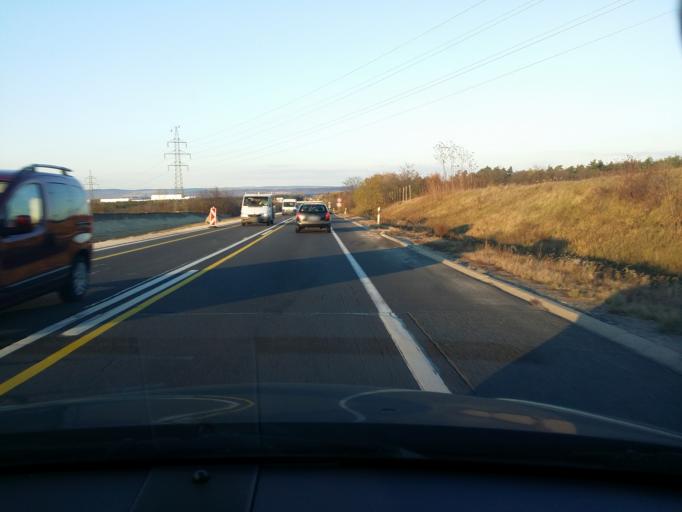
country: HU
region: Pest
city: God
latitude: 47.6628
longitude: 19.1628
